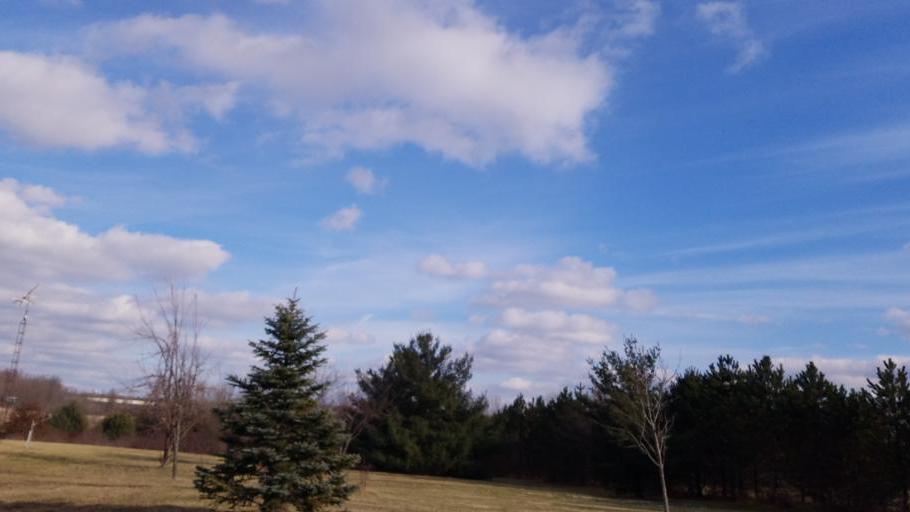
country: US
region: Ohio
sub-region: Crawford County
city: Crestline
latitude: 40.7740
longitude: -82.6790
